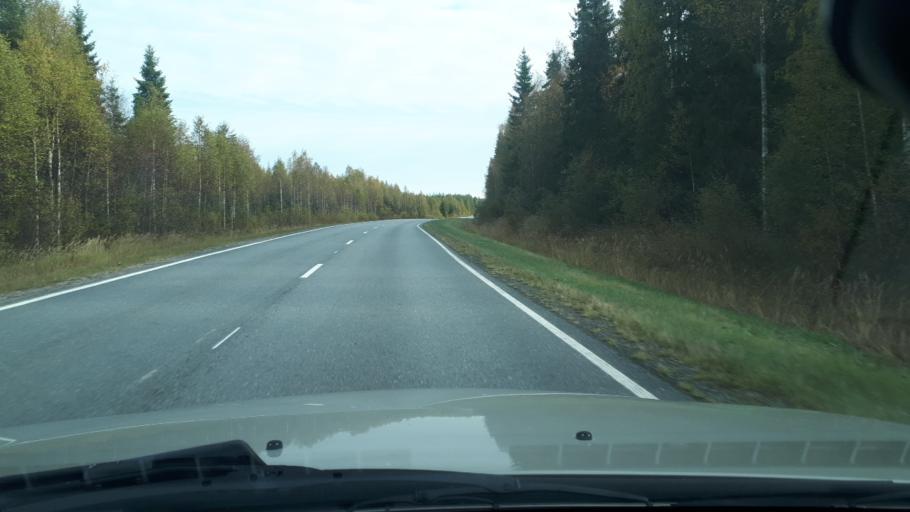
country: FI
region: Lapland
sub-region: Rovaniemi
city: Ranua
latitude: 65.9773
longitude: 26.1217
